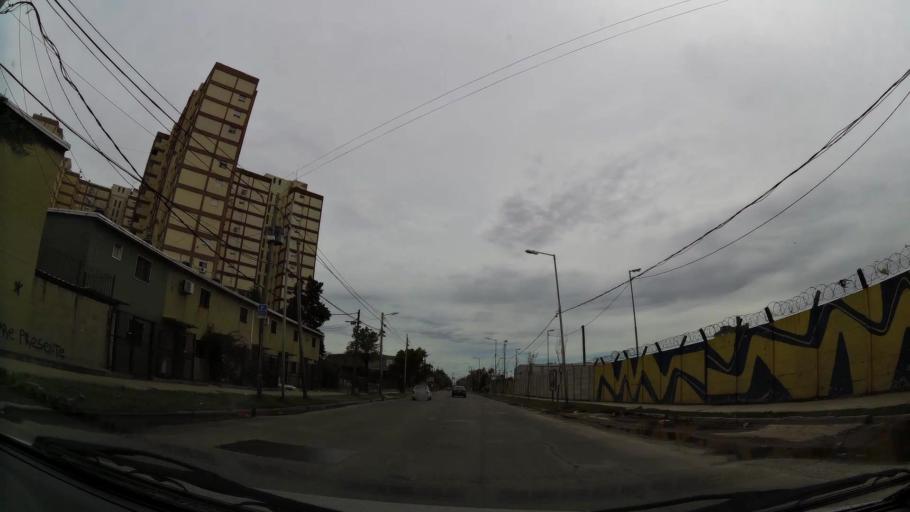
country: AR
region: Buenos Aires
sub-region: Partido de Avellaneda
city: Avellaneda
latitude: -34.6599
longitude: -58.3438
